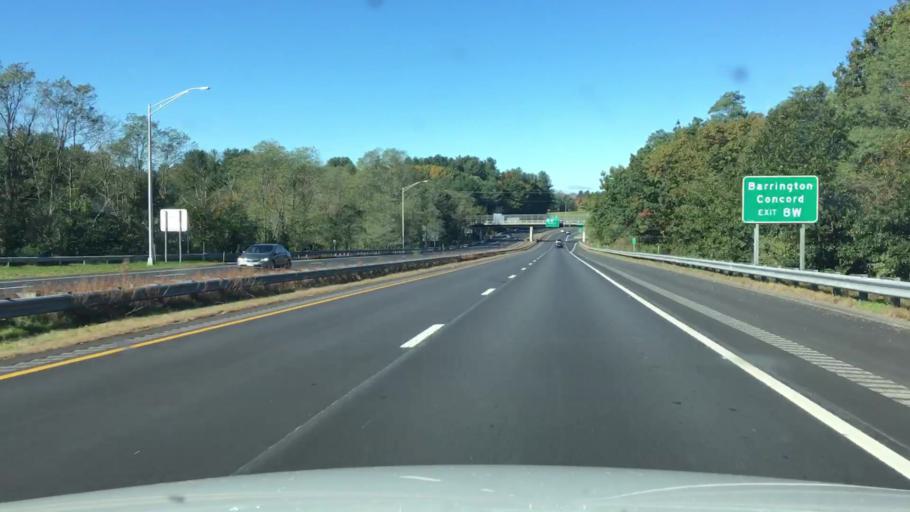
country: US
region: New Hampshire
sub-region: Strafford County
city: Dover
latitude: 43.1821
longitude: -70.8791
